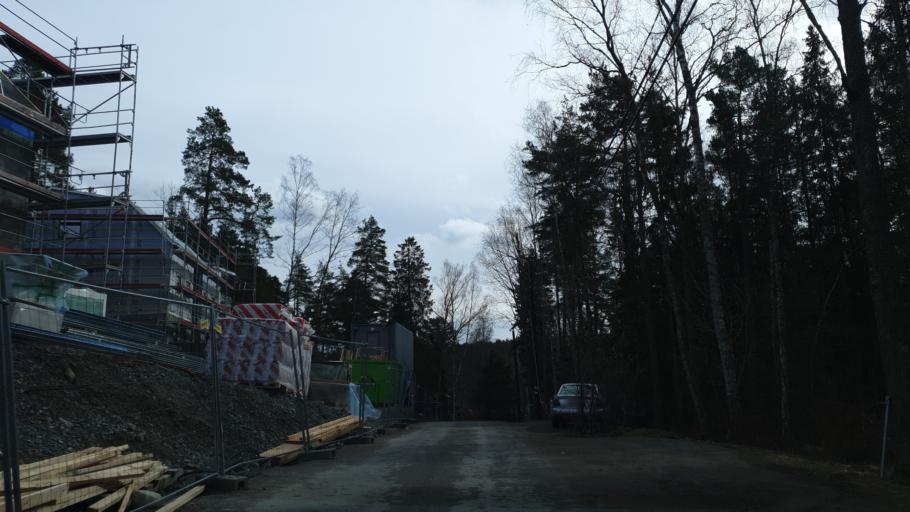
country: SE
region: Stockholm
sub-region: Nacka Kommun
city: Boo
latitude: 59.3316
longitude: 18.2911
